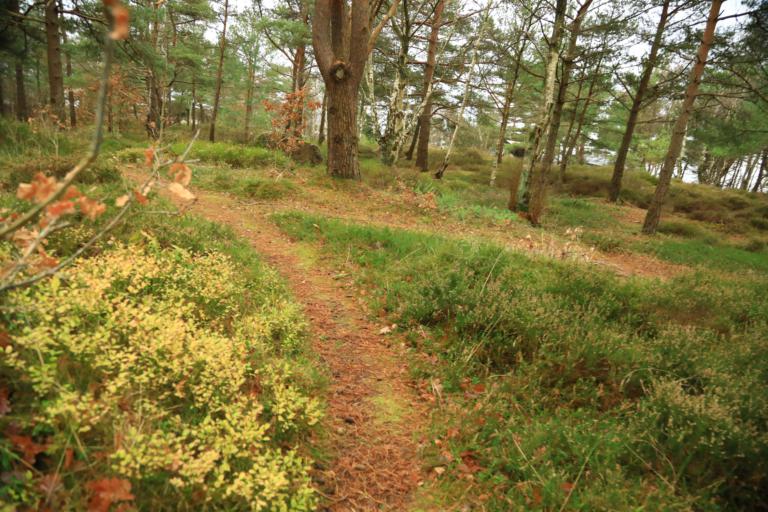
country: SE
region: Halland
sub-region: Varbergs Kommun
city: Varberg
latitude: 57.1716
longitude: 12.2101
